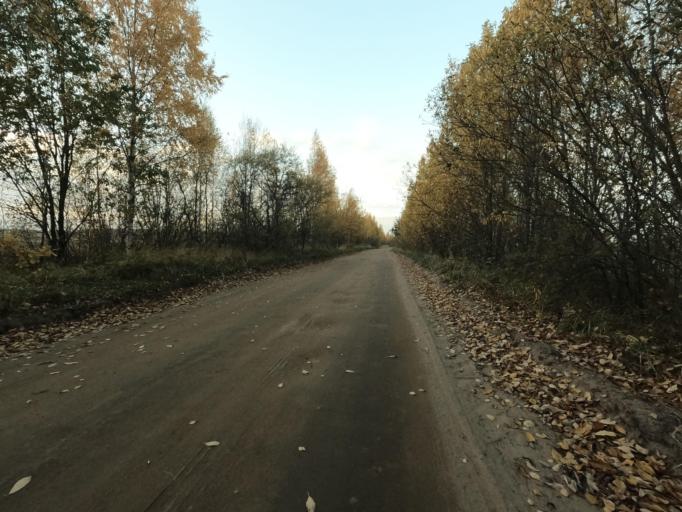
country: RU
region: Leningrad
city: Mga
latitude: 59.7950
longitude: 31.2006
